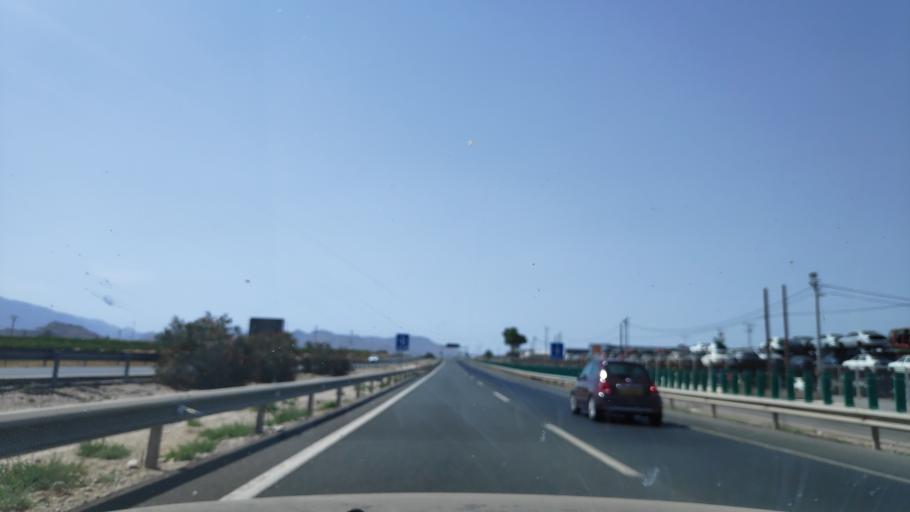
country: ES
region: Murcia
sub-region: Murcia
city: Lorqui
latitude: 38.1169
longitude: -1.2429
